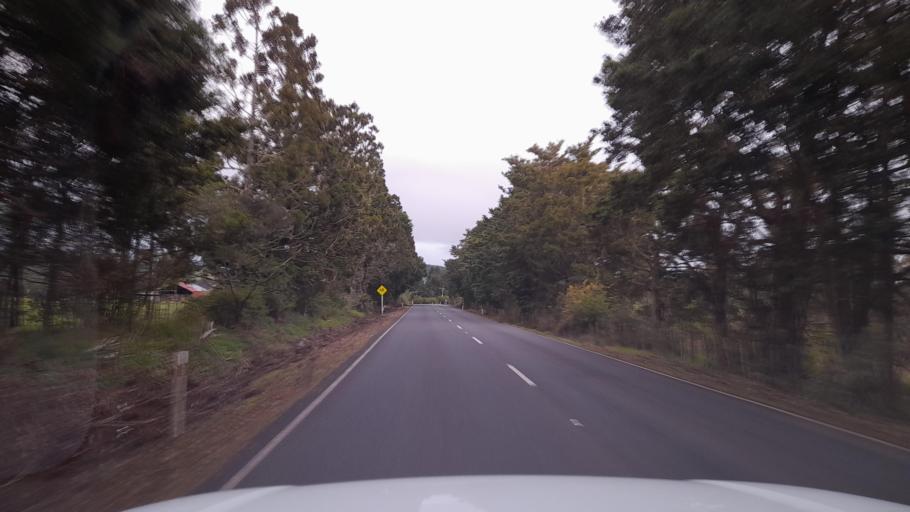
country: NZ
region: Northland
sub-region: Far North District
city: Waimate North
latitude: -35.5849
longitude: 173.8406
